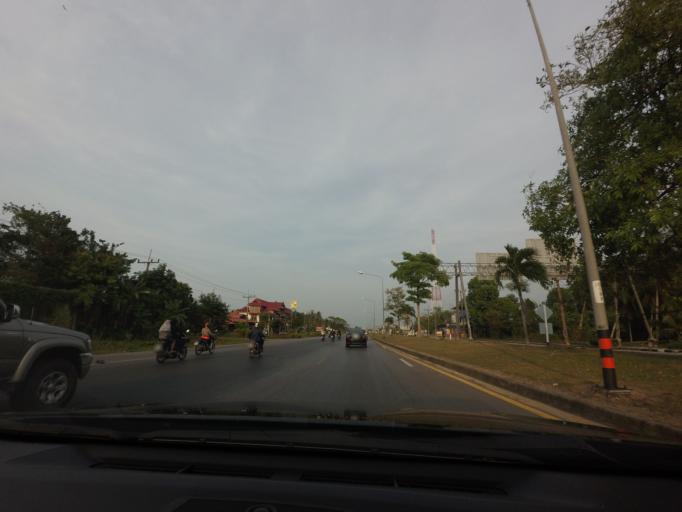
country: TH
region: Pattani
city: Pattani
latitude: 6.8707
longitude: 101.2833
